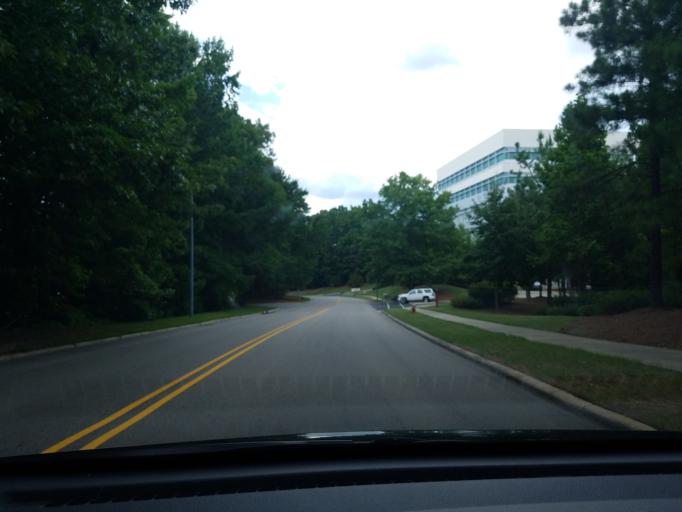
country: US
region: North Carolina
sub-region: Wake County
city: Apex
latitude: 35.7348
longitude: -78.8042
